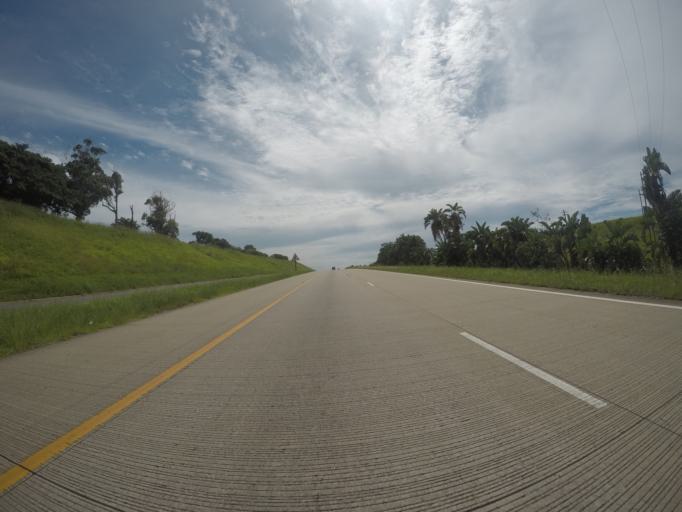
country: ZA
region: KwaZulu-Natal
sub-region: iLembe District Municipality
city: Stanger
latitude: -29.3442
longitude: 31.3261
